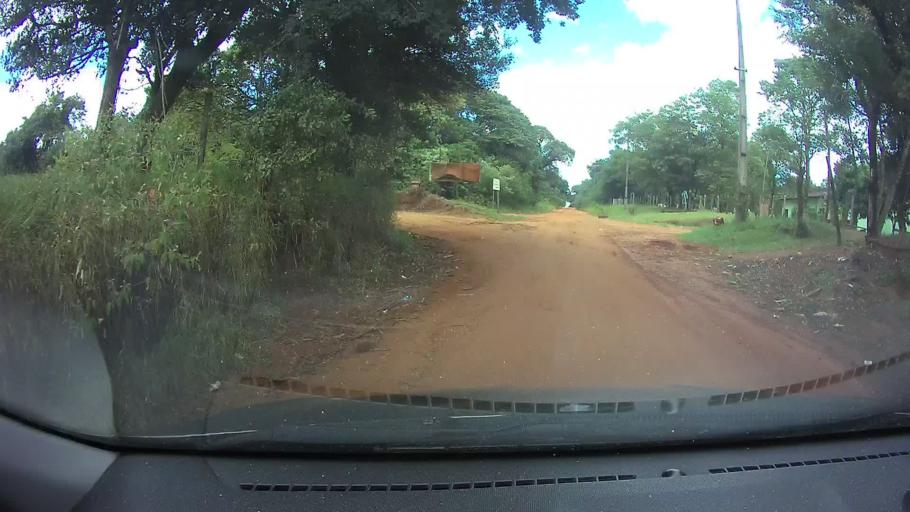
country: PY
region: Paraguari
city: La Colmena
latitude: -25.9434
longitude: -56.7795
